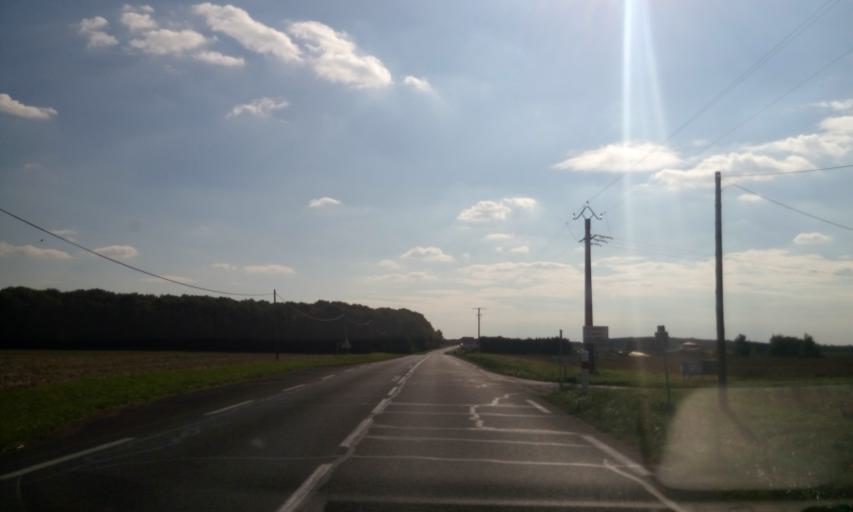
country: FR
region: Centre
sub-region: Departement d'Indre-et-Loire
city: Poce-sur-Cisse
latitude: 47.4821
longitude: 1.0083
